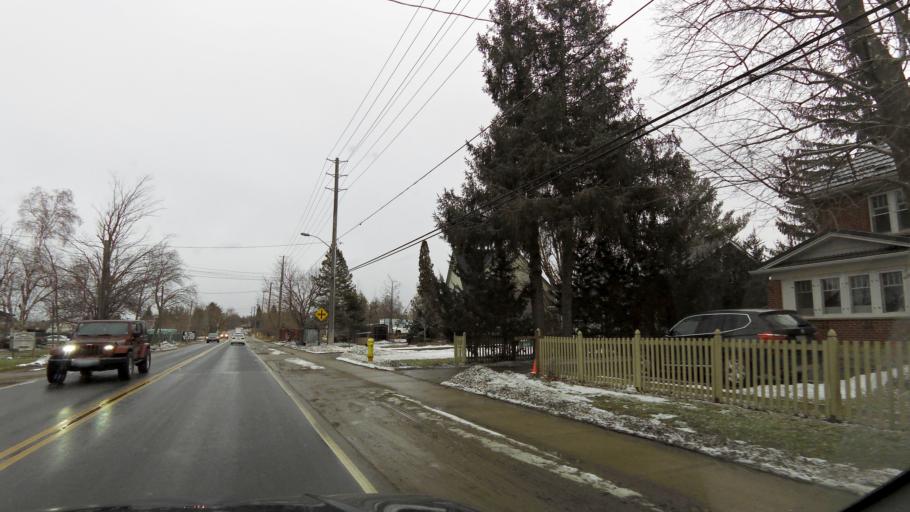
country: CA
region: Ontario
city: Vaughan
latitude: 43.8418
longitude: -79.6598
